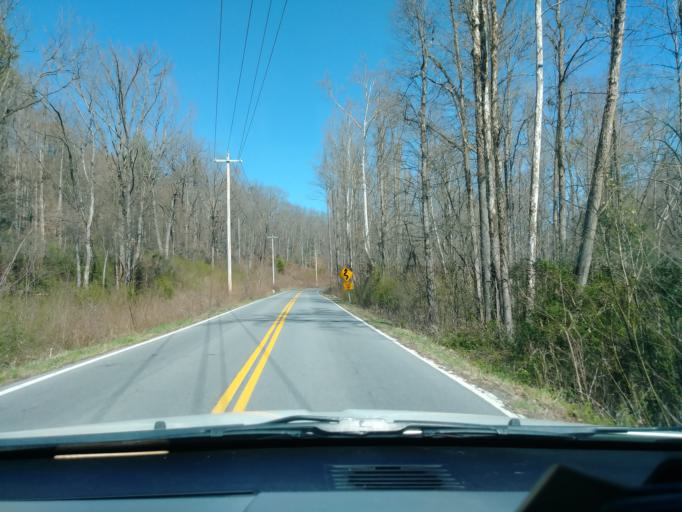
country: US
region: Tennessee
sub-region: Cocke County
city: Newport
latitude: 35.9495
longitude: -83.0537
